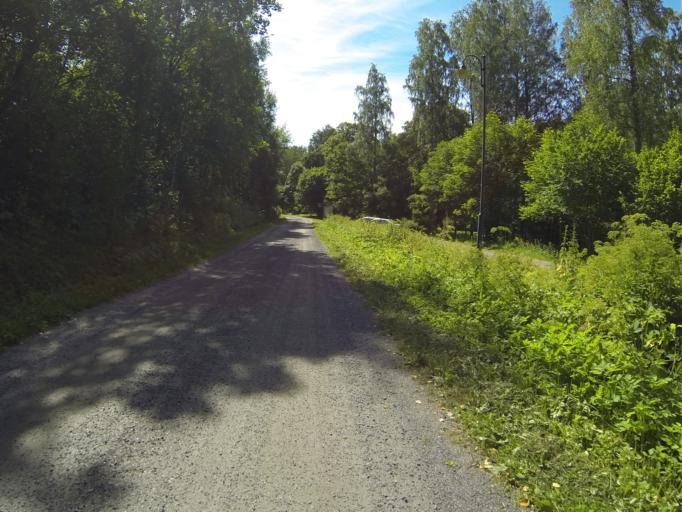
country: FI
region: Varsinais-Suomi
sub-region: Salo
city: Halikko
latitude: 60.2731
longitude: 22.9929
